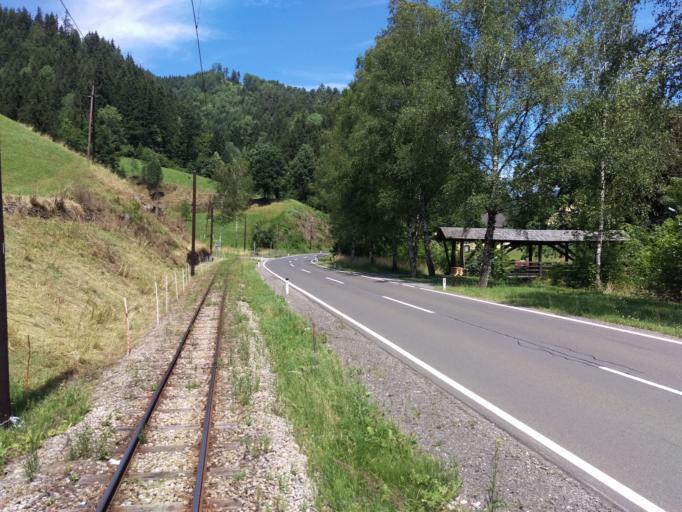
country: AT
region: Styria
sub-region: Politischer Bezirk Bruck-Muerzzuschlag
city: Pernegg an der Mur
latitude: 47.3796
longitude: 15.4002
